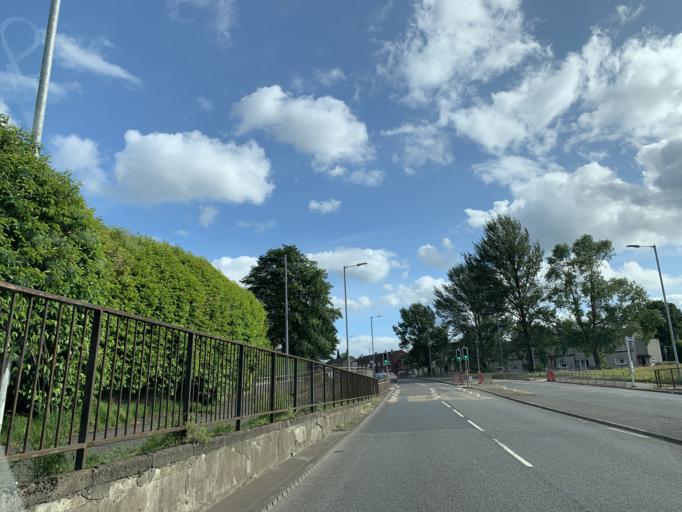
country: GB
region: Scotland
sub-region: Renfrewshire
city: Renfrew
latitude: 55.8551
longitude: -4.3644
